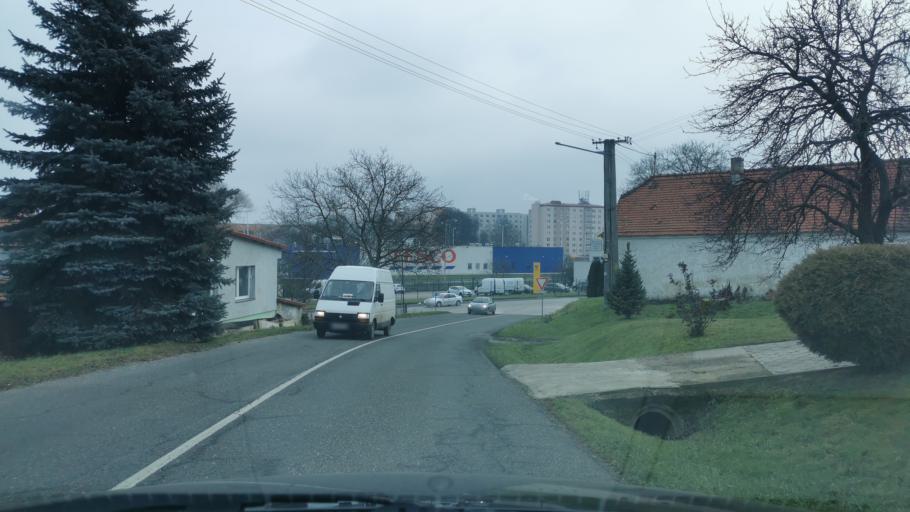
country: SK
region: Trnavsky
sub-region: Okres Senica
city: Senica
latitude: 48.6900
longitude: 17.3649
